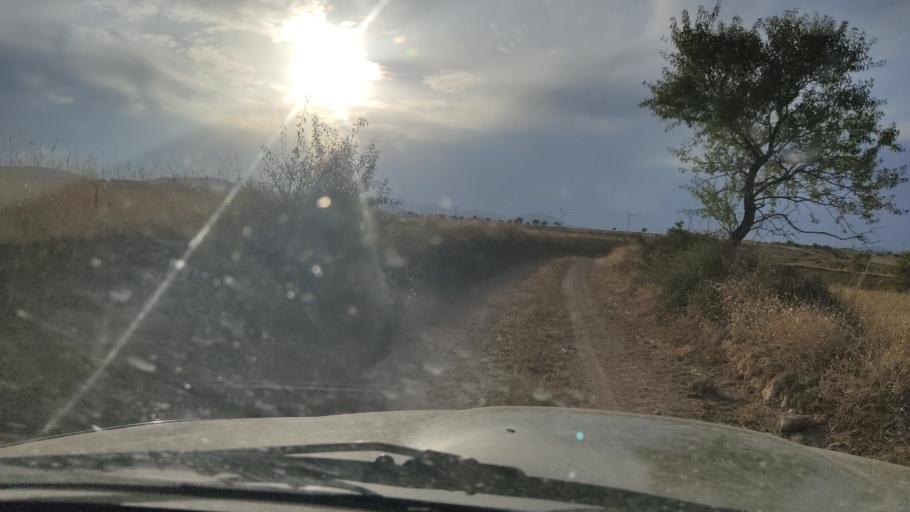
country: ES
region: Aragon
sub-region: Provincia de Teruel
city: Monforte de Moyuela
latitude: 41.0660
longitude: -0.9874
